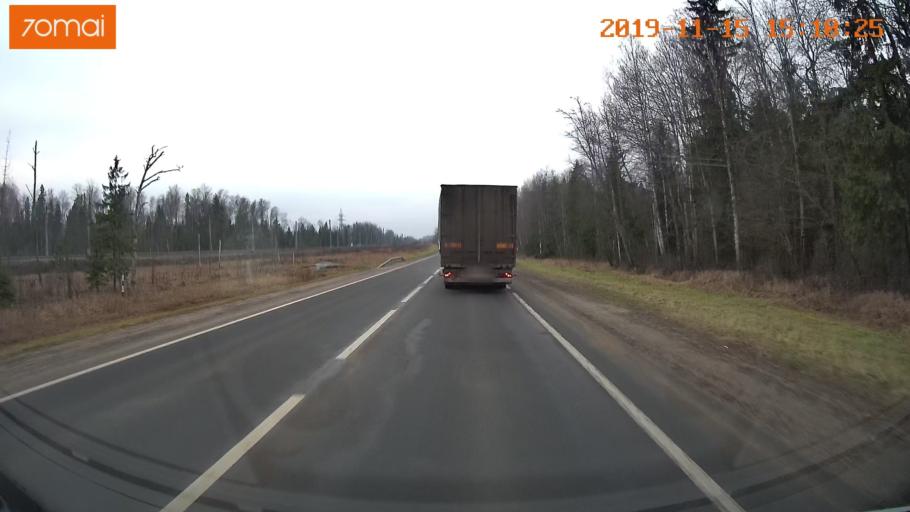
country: RU
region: Jaroslavl
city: Prechistoye
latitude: 58.3480
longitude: 40.2541
